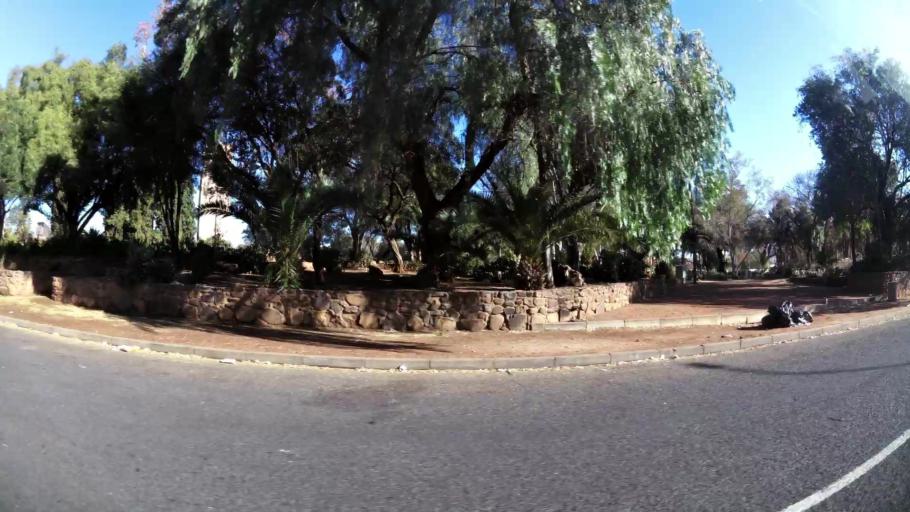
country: ZA
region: Northern Cape
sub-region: Frances Baard District Municipality
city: Kimberley
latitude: -28.7440
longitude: 24.7683
